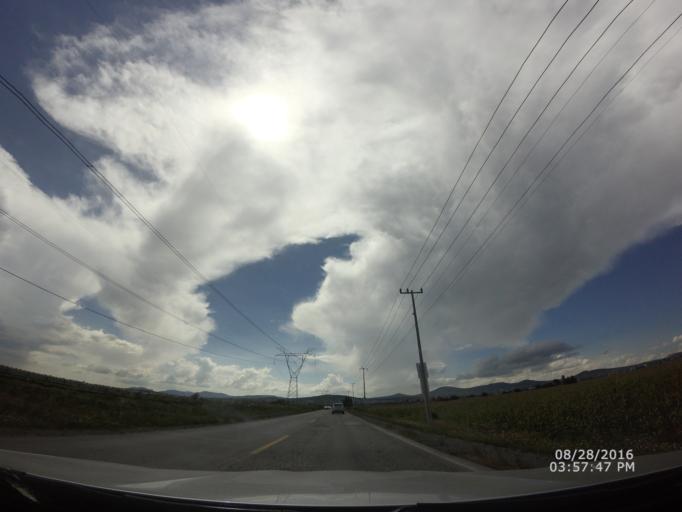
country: MX
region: Hidalgo
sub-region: Mineral de la Reforma
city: La Colonia
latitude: 20.0358
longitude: -98.7712
